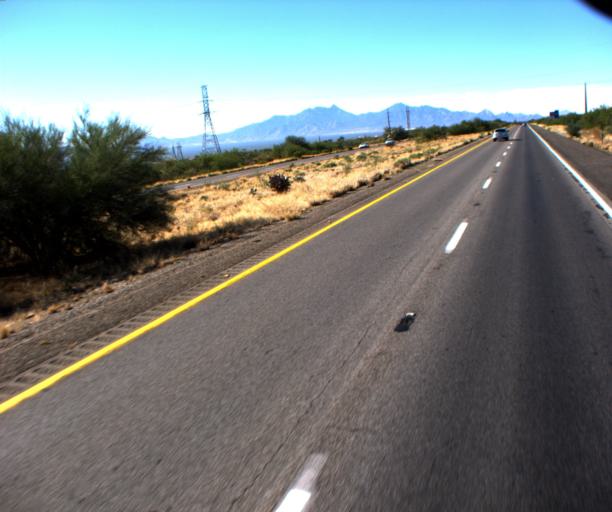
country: US
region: Arizona
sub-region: Pima County
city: Sahuarita
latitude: 31.9760
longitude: -110.9903
